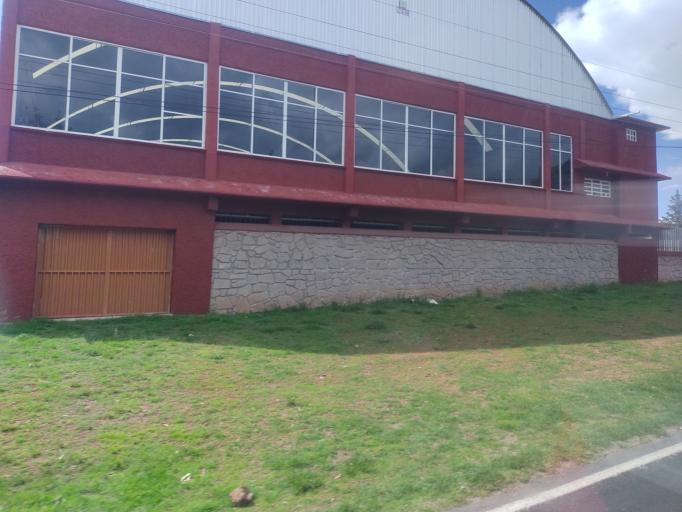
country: MX
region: Mexico
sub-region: Aculco
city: El Colorado
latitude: 20.0926
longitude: -99.7715
